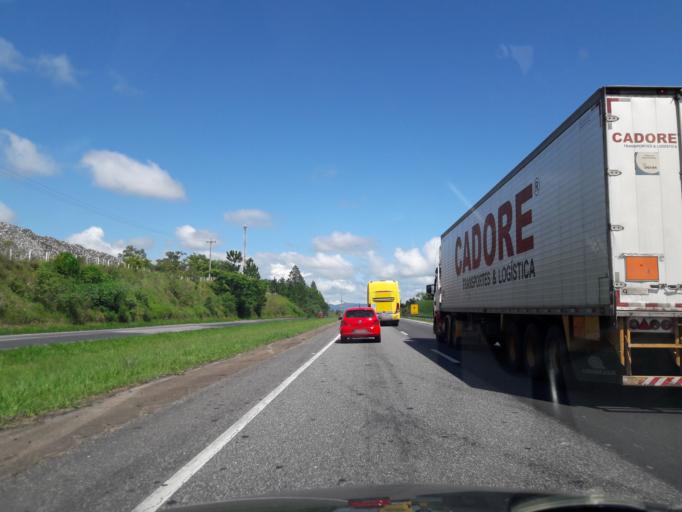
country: BR
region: Sao Paulo
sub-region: Cajati
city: Cajati
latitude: -24.7222
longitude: -48.0631
